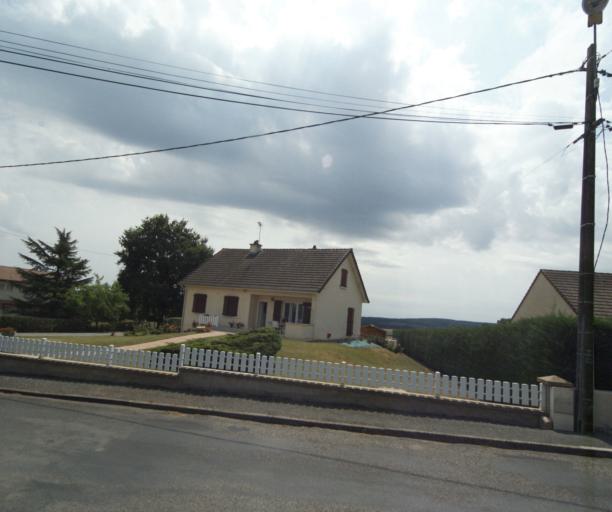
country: FR
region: Bourgogne
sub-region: Departement de Saone-et-Loire
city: Gueugnon
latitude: 46.6011
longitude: 4.0205
